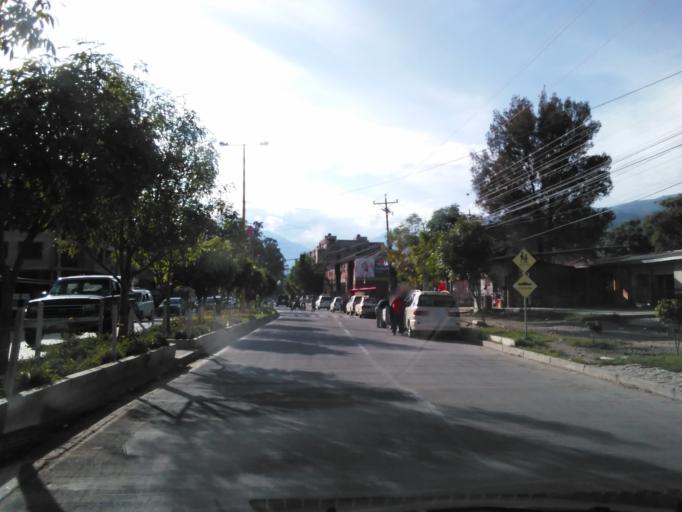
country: BO
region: Cochabamba
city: Cochabamba
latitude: -17.3456
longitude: -66.2036
